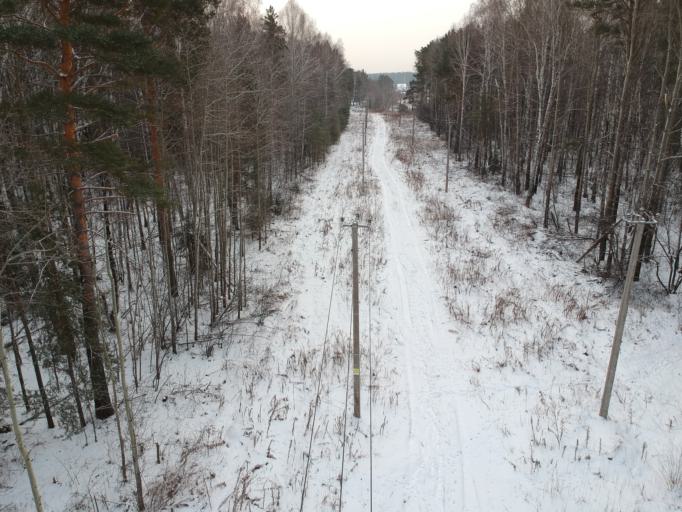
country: RU
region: Sverdlovsk
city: Zavodouspenskoye
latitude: 57.0888
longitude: 65.1552
